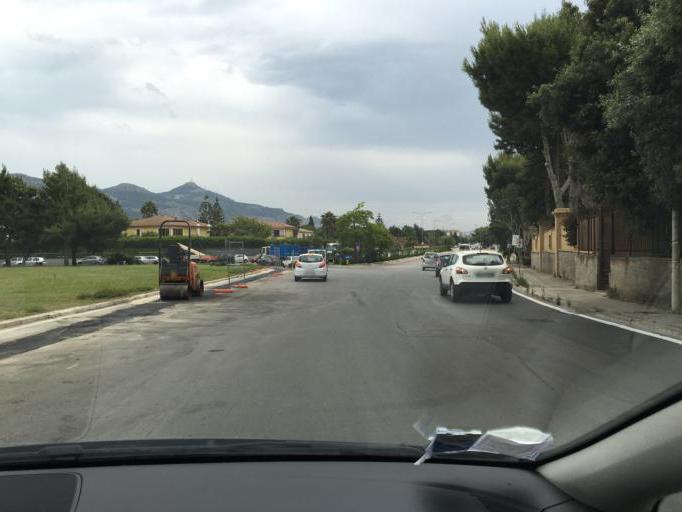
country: IT
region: Sicily
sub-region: Palermo
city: Isola delle Femmine
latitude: 38.1886
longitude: 13.2993
